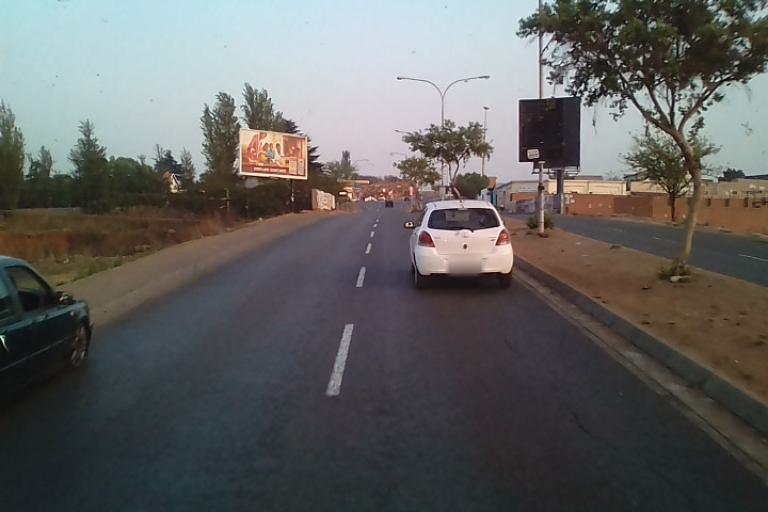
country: ZA
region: Gauteng
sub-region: City of Johannesburg Metropolitan Municipality
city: Soweto
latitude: -26.2337
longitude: 27.8761
